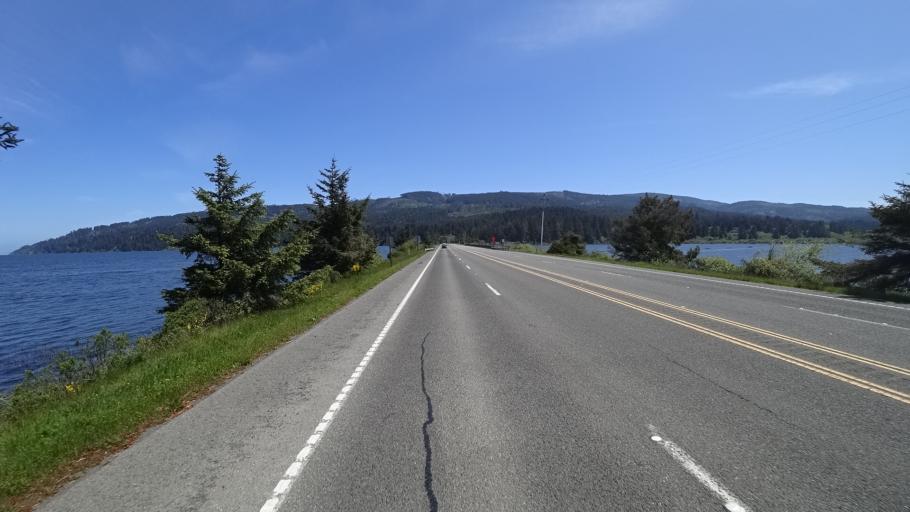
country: US
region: California
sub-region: Humboldt County
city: Westhaven-Moonstone
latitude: 41.1618
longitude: -124.1129
